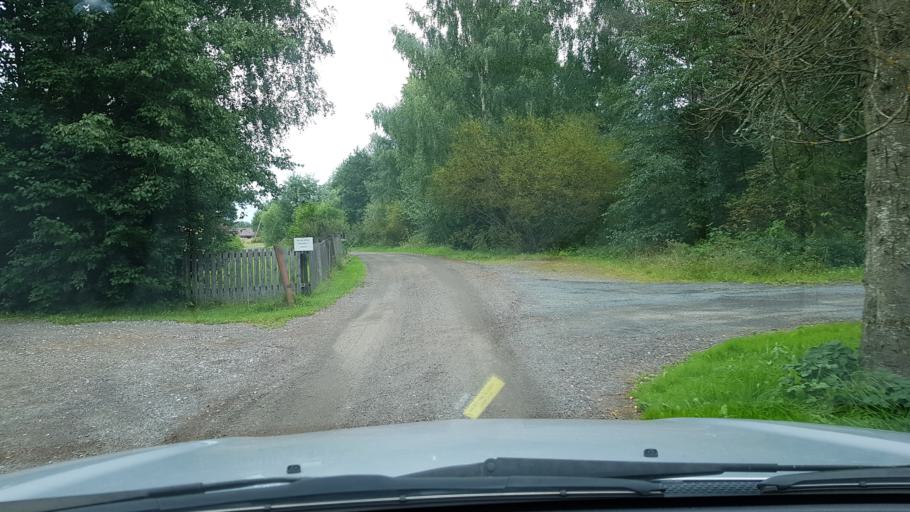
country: EE
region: Harju
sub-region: Rae vald
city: Jueri
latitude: 59.3726
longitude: 24.9459
